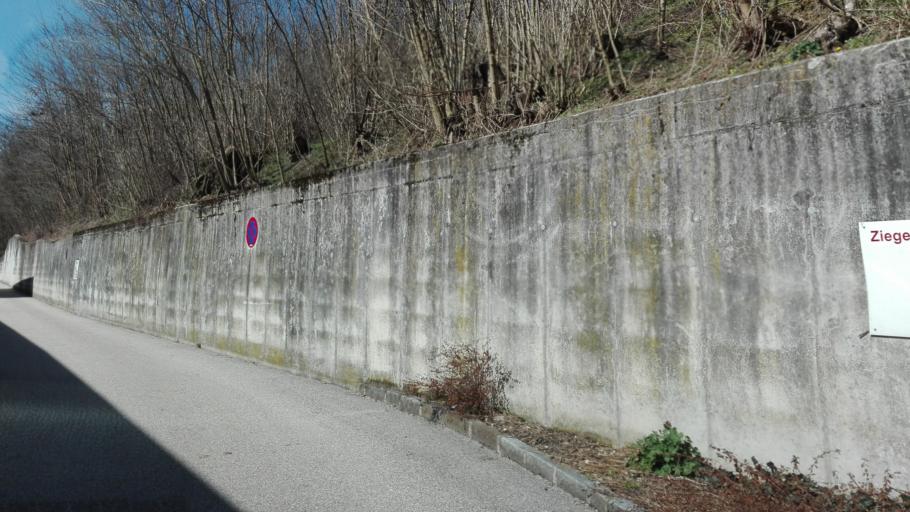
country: AT
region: Upper Austria
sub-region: Politischer Bezirk Grieskirchen
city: Grieskirchen
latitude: 48.2328
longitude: 13.8417
